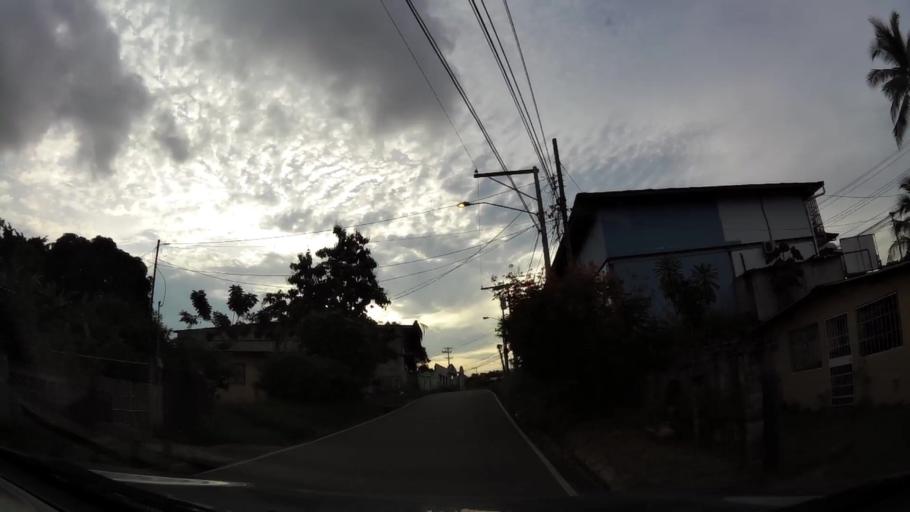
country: PA
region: Panama
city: Tocumen
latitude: 9.1019
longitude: -79.3837
